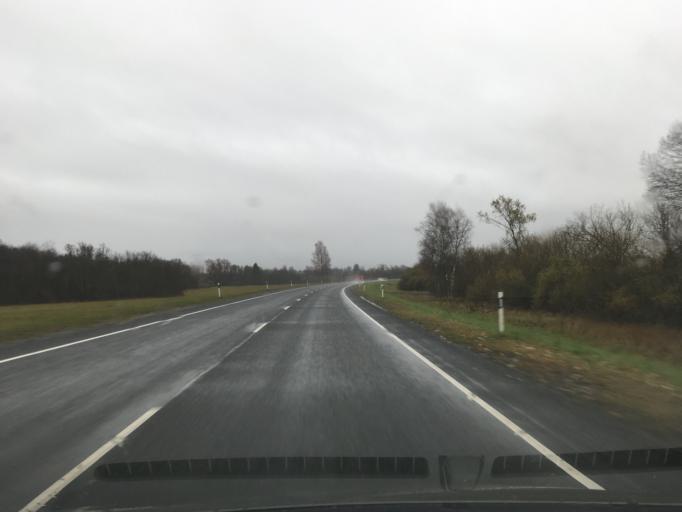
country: EE
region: Harju
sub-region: Nissi vald
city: Turba
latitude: 58.9247
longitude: 24.1109
